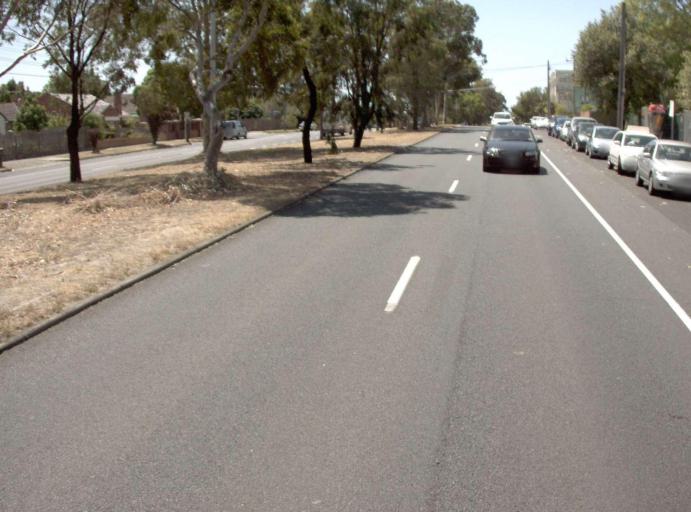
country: AU
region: Victoria
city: McKinnon
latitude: -37.9292
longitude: 145.0576
